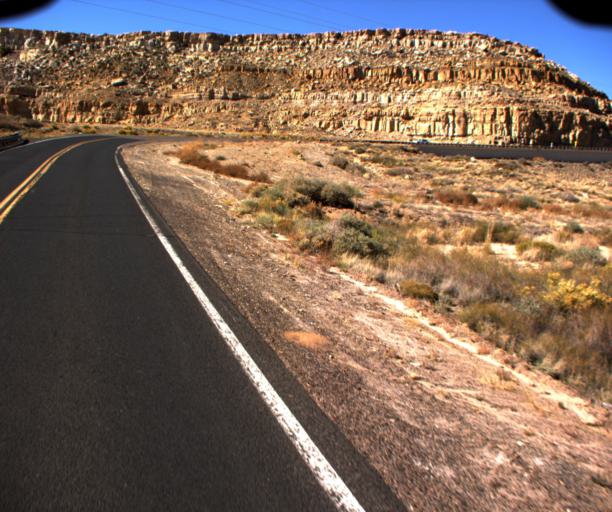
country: US
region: Arizona
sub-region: Navajo County
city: First Mesa
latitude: 35.8064
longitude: -110.5194
